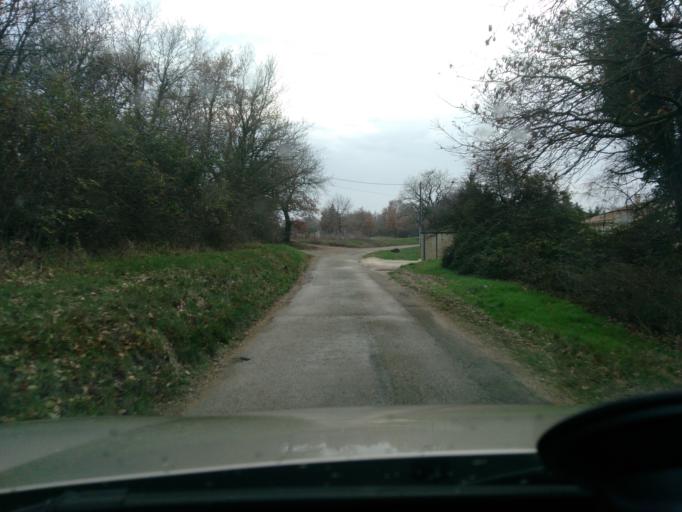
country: FR
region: Rhone-Alpes
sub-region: Departement de la Drome
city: Montelimar
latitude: 44.5725
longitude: 4.7699
